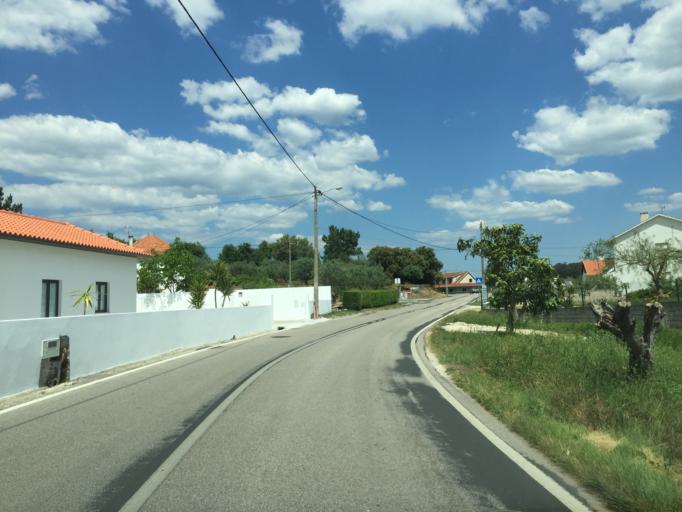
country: PT
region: Santarem
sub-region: Ourem
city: Ourem
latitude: 39.6441
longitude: -8.6129
